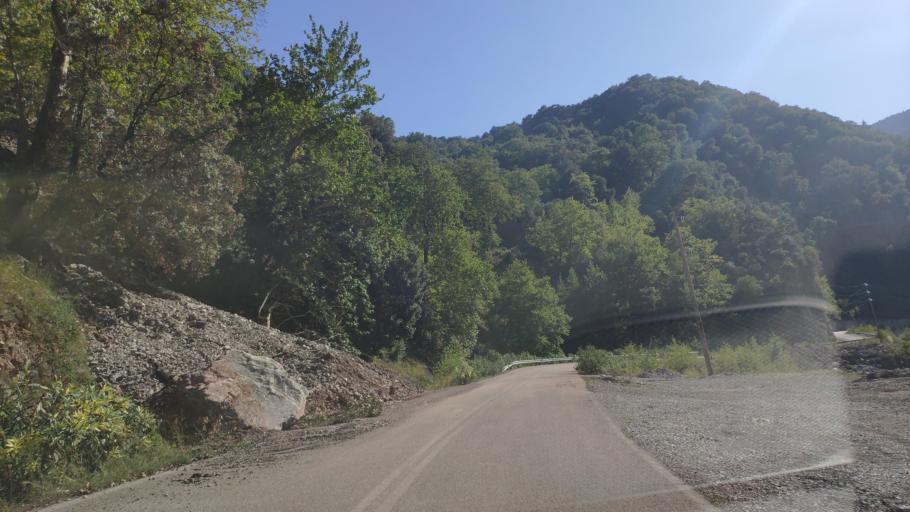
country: GR
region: Central Greece
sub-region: Nomos Evrytanias
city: Kerasochori
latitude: 39.0520
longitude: 21.6029
